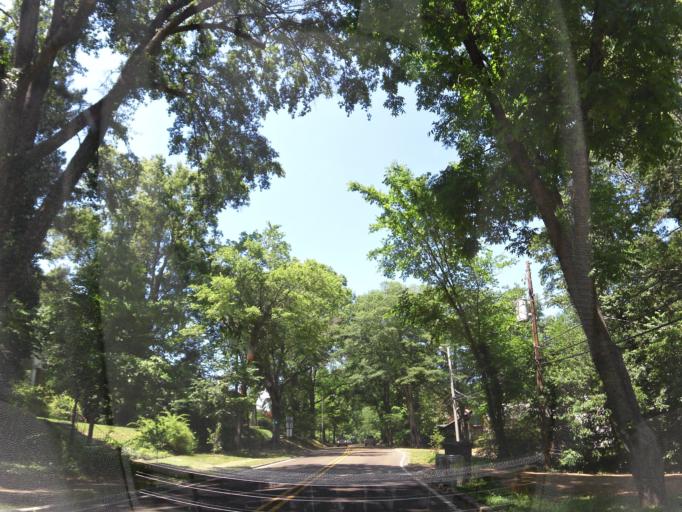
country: US
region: Mississippi
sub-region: Lafayette County
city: Oxford
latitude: 34.3589
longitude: -89.5203
